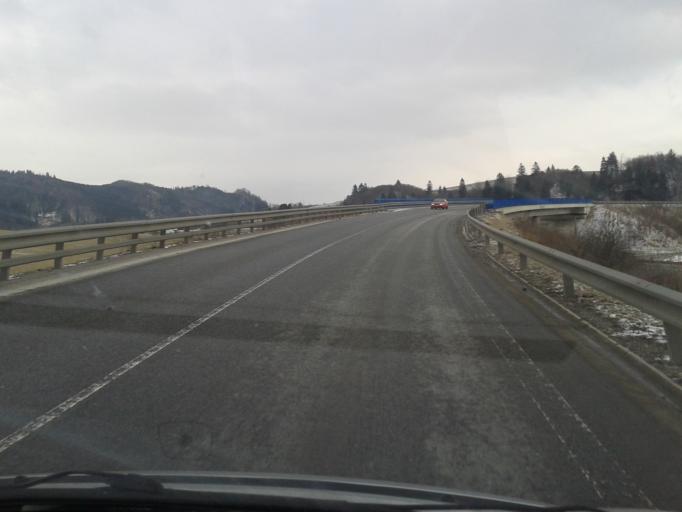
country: SK
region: Zilinsky
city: Tvrdosin
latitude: 49.3459
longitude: 19.5712
